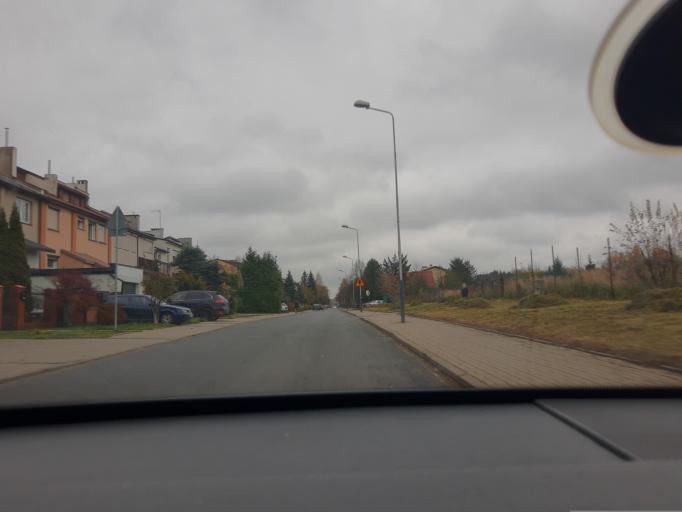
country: PL
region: Lodz Voivodeship
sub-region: Powiat pabianicki
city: Konstantynow Lodzki
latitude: 51.7418
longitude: 19.3738
